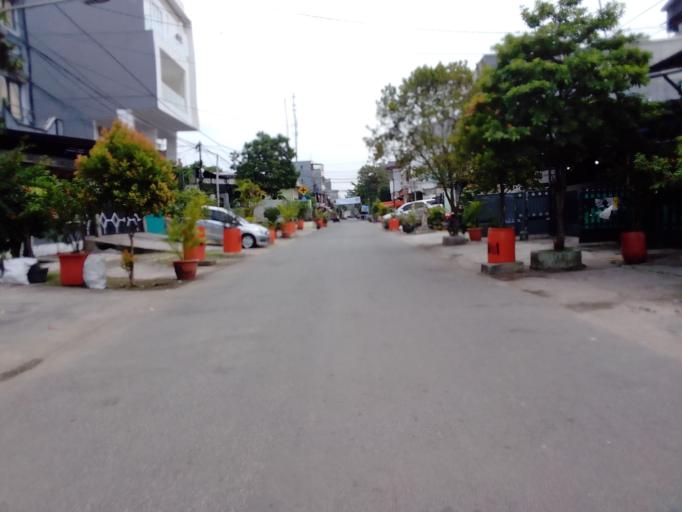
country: ID
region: Jakarta Raya
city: Jakarta
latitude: -6.1554
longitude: 106.8155
